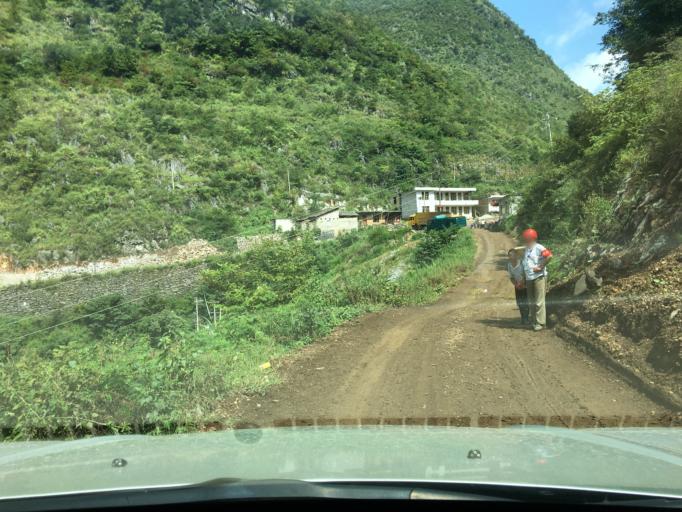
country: CN
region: Guizhou Sheng
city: Liupanshui
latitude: 25.9097
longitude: 105.0997
